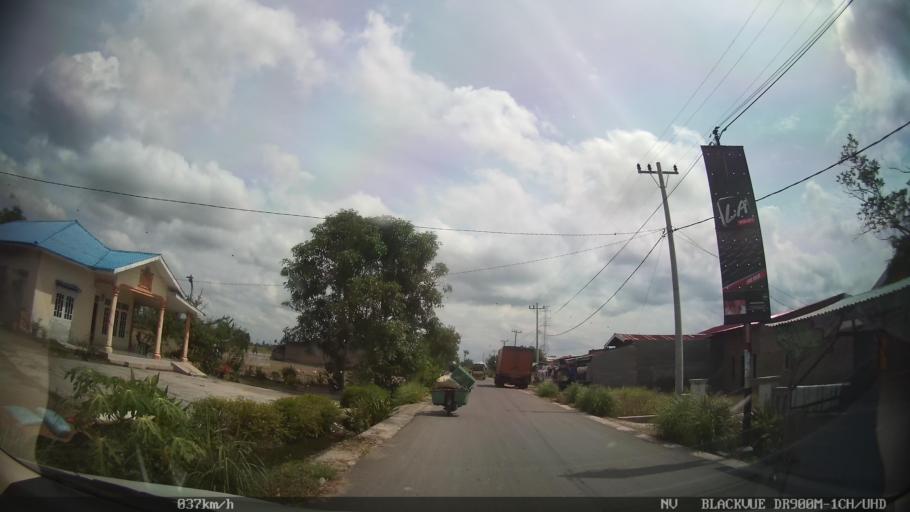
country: ID
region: North Sumatra
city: Percut
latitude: 3.5758
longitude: 98.8409
